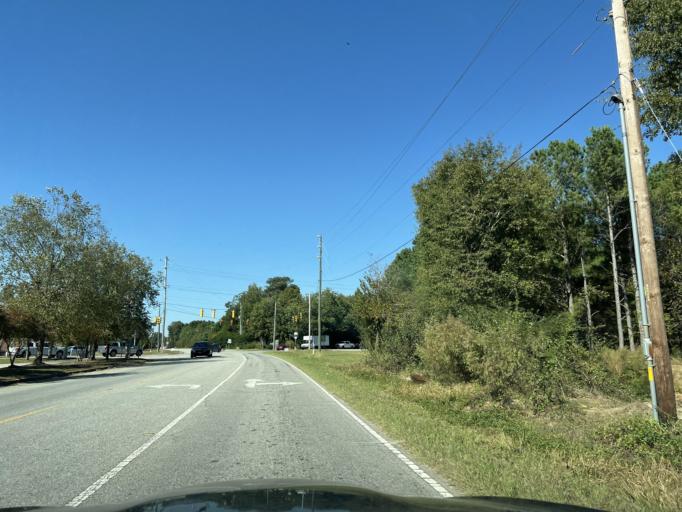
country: US
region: North Carolina
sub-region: Johnston County
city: Clayton
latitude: 35.6682
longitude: -78.4760
